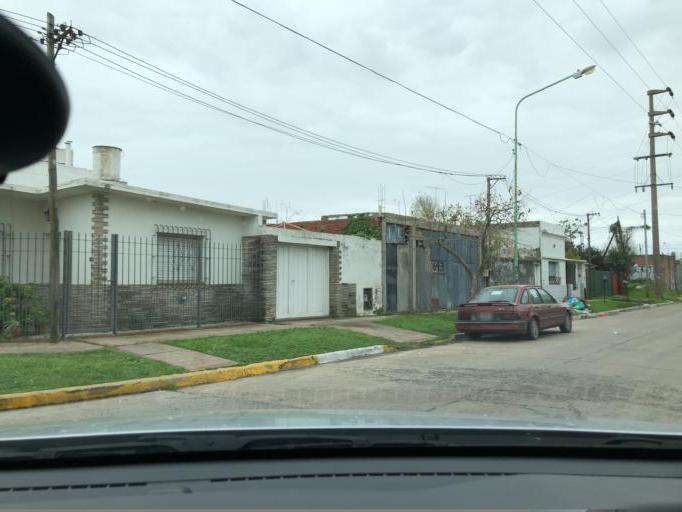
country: AR
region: Buenos Aires
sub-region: Partido de Ensenada
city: Ensenada
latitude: -34.8604
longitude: -57.9148
